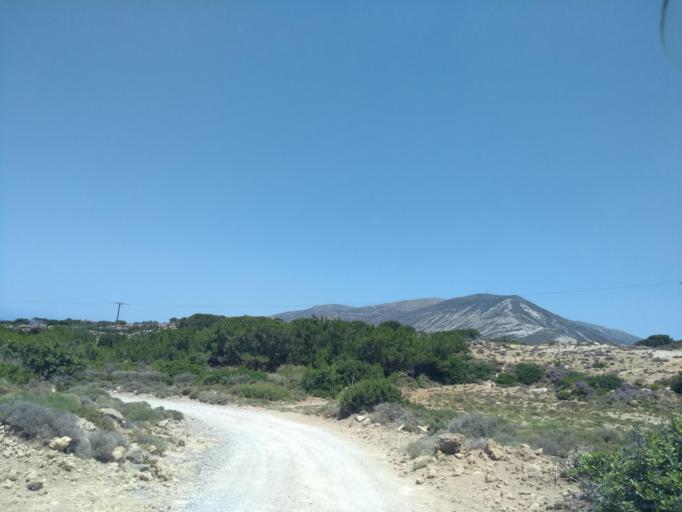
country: GR
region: Crete
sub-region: Nomos Chanias
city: Vryses
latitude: 35.3134
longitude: 23.5364
